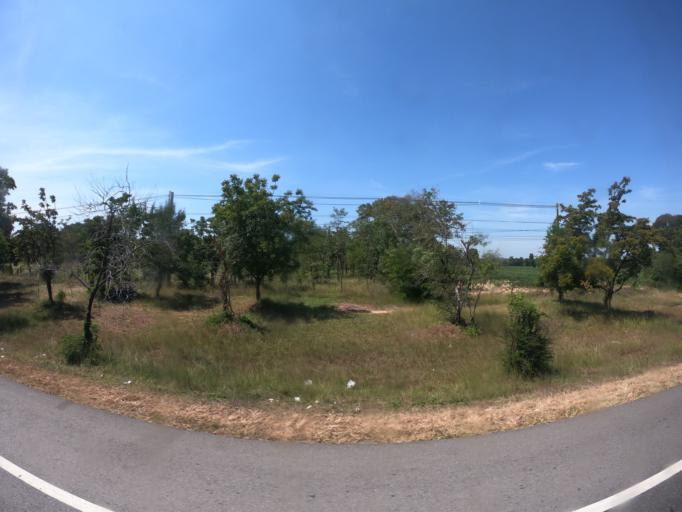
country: TH
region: Khon Kaen
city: Phon
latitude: 15.7735
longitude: 102.6066
